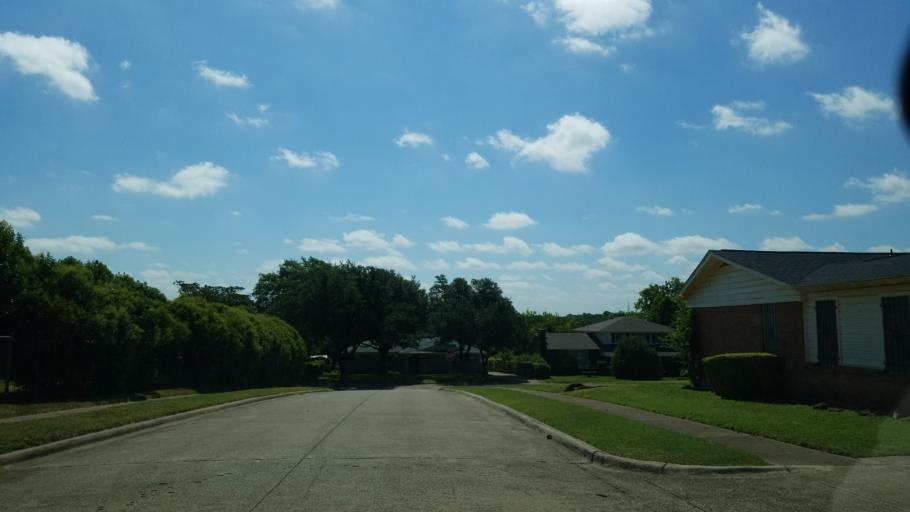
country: US
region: Texas
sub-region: Dallas County
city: Dallas
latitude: 32.7274
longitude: -96.7954
